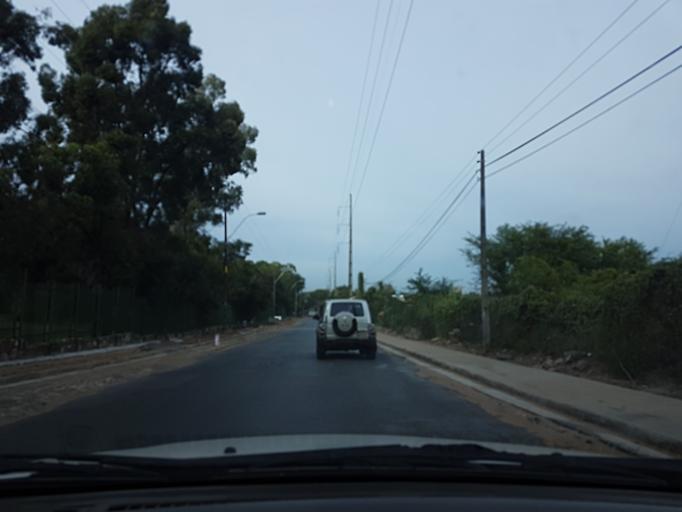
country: PY
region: Asuncion
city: Asuncion
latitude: -25.2486
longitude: -57.5790
